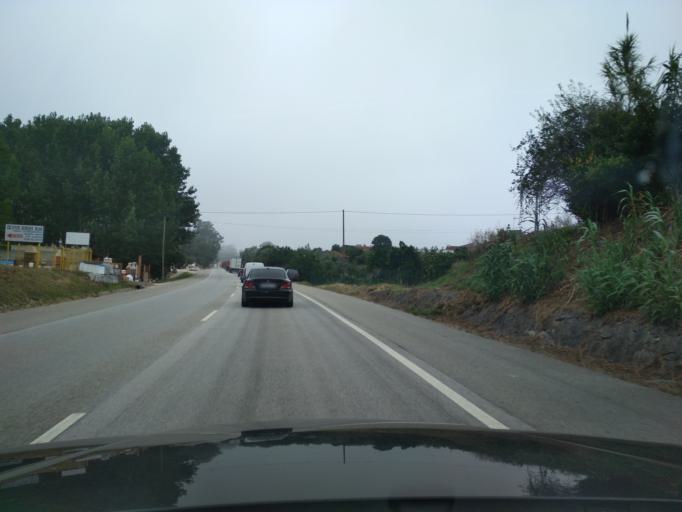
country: PT
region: Aveiro
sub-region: Mealhada
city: Pampilhosa do Botao
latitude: 40.3168
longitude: -8.4519
